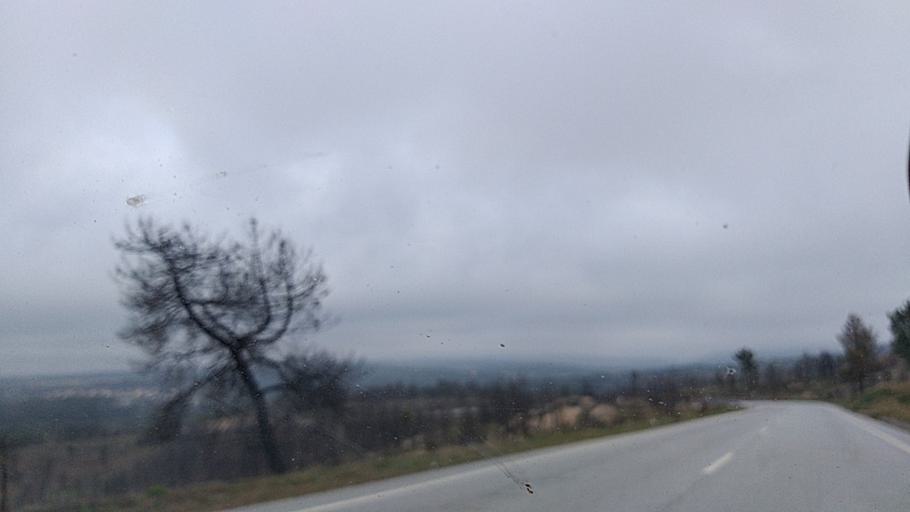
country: PT
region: Guarda
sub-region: Fornos de Algodres
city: Fornos de Algodres
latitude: 40.7036
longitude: -7.4836
